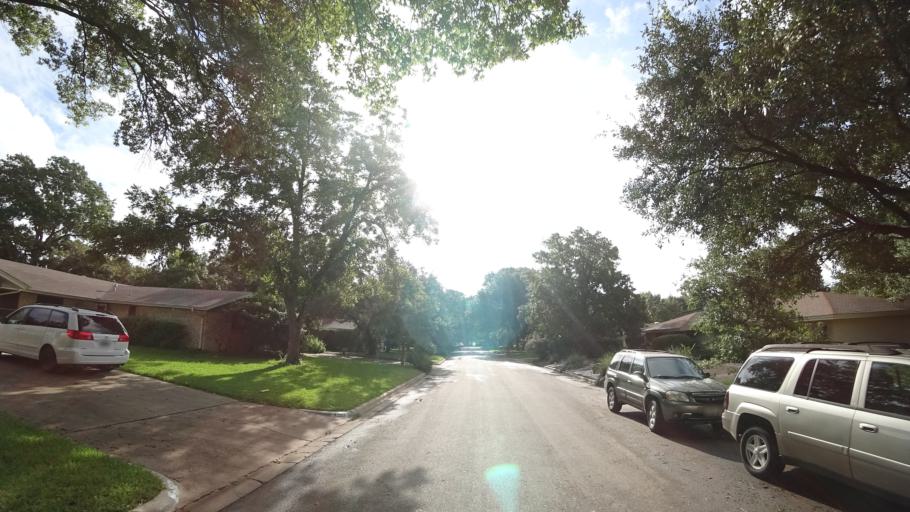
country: US
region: Texas
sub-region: Travis County
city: West Lake Hills
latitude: 30.3558
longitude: -97.7431
